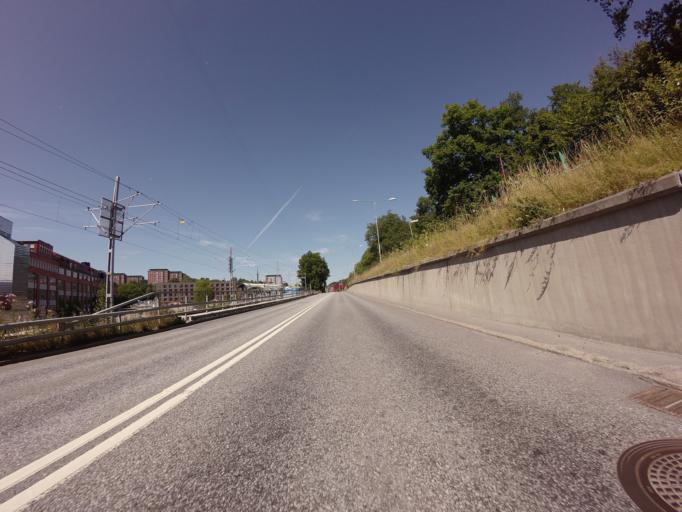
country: SE
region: Stockholm
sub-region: Lidingo
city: Lidingoe
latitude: 59.3459
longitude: 18.1583
